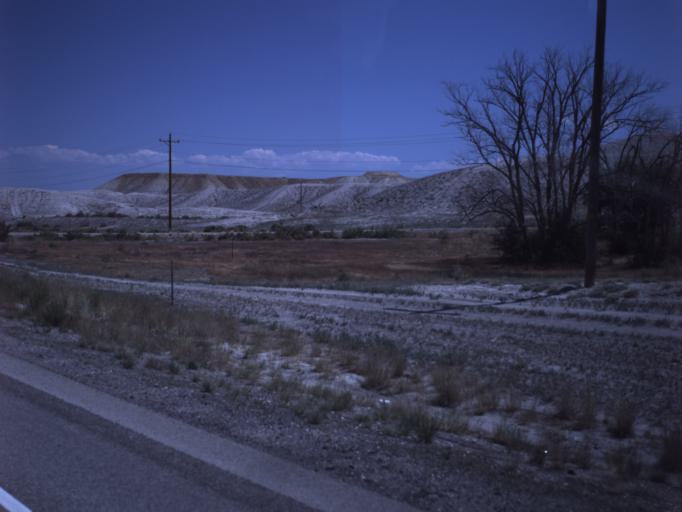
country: US
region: Utah
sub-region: Emery County
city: Ferron
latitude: 39.1451
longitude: -111.0949
